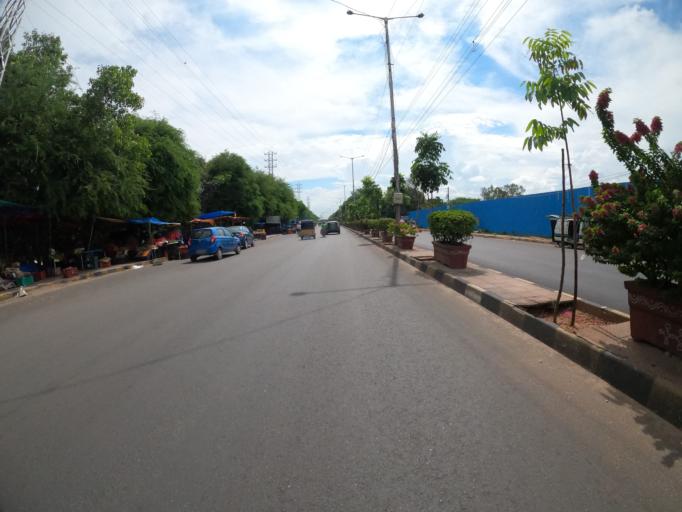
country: IN
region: Telangana
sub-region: Hyderabad
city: Hyderabad
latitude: 17.3731
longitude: 78.4107
